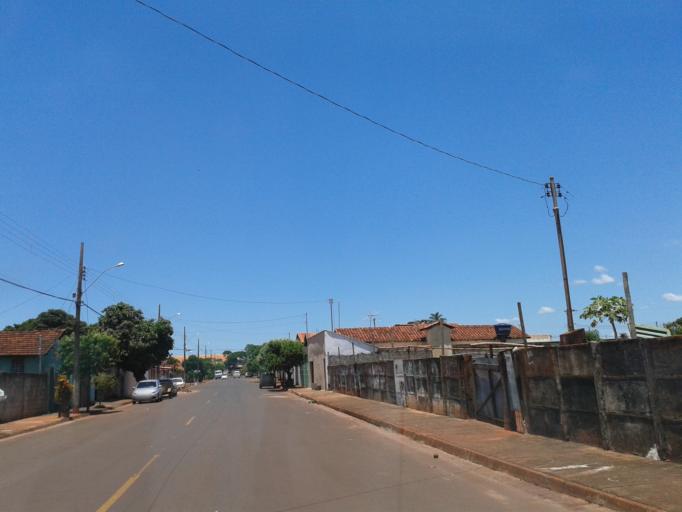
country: BR
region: Minas Gerais
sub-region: Centralina
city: Centralina
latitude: -18.7246
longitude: -49.1969
